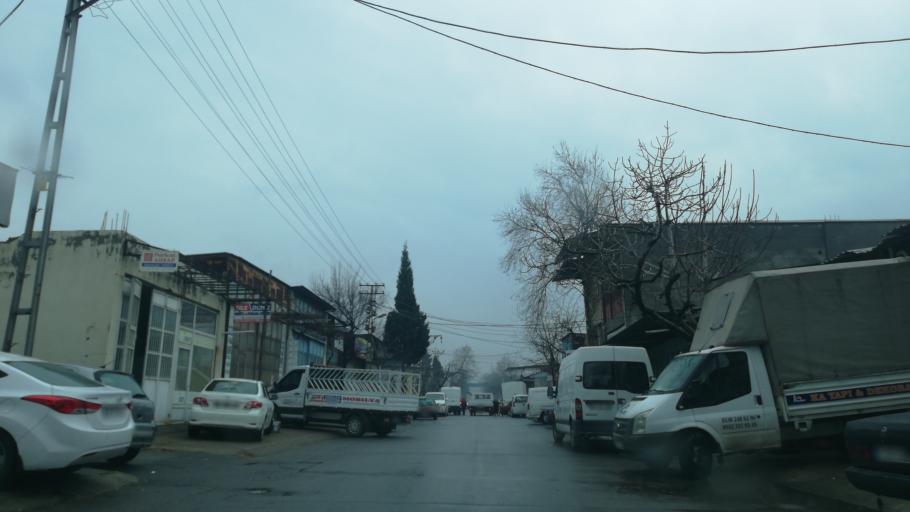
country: TR
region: Kahramanmaras
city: Kahramanmaras
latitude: 37.5619
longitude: 36.9590
